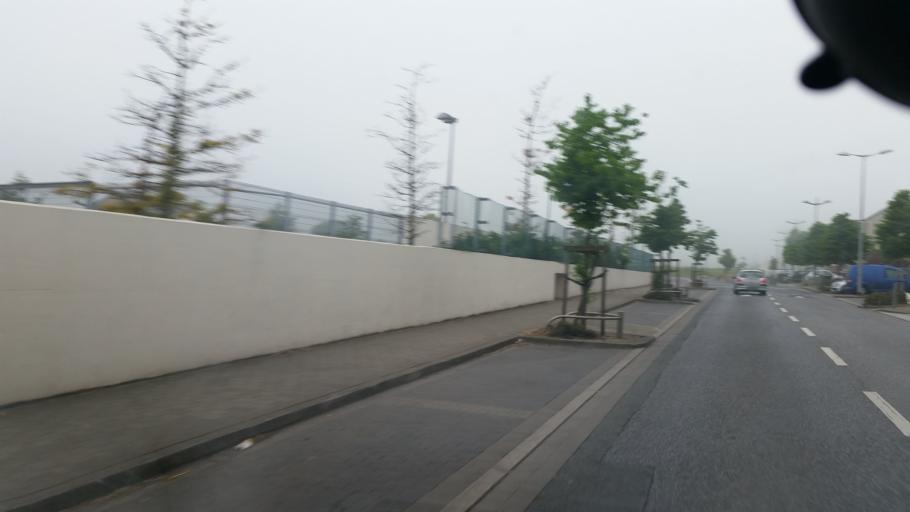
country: IE
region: Leinster
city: Ballymun
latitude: 53.4038
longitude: -6.2750
